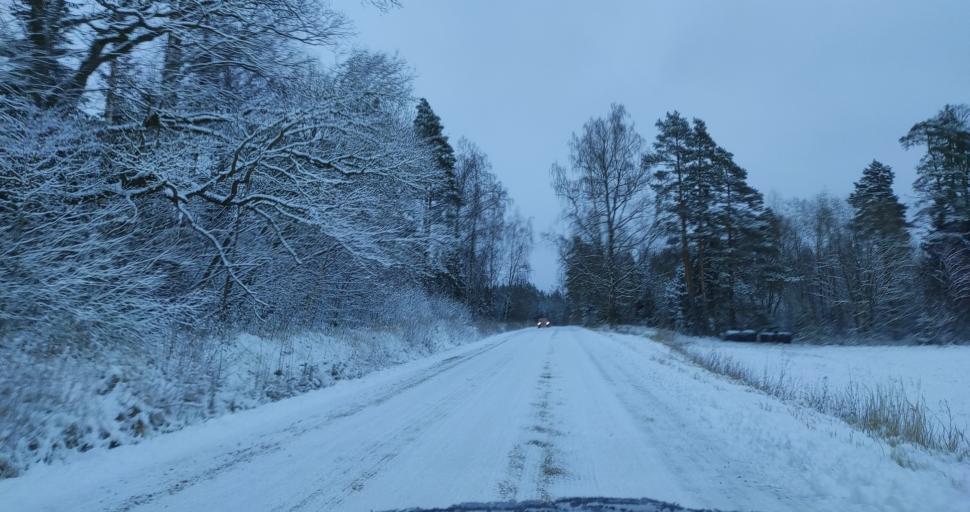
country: LV
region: Kuldigas Rajons
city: Kuldiga
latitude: 56.9513
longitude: 21.7595
